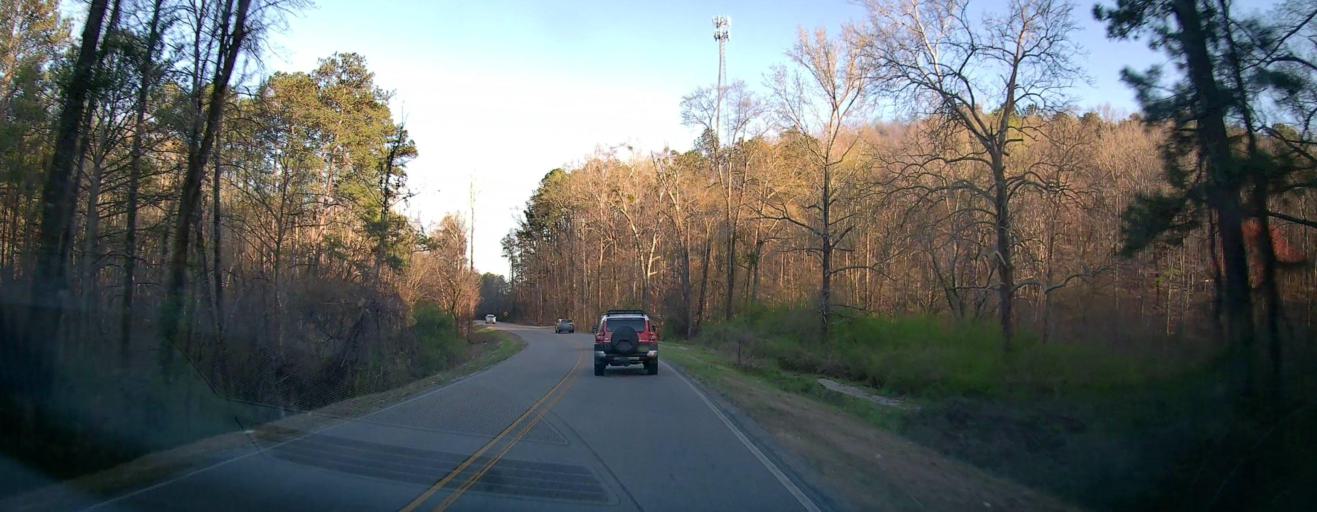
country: US
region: Alabama
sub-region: Shelby County
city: Chelsea
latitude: 33.3506
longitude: -86.6461
